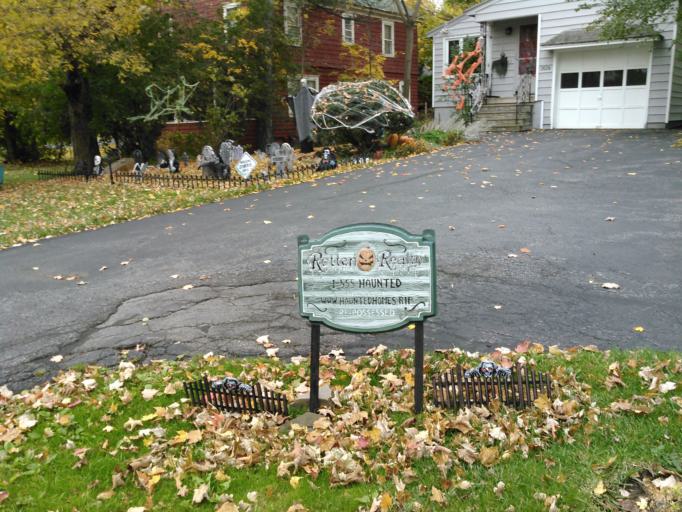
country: US
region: New York
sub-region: Onondaga County
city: Syracuse
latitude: 43.0222
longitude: -76.1137
